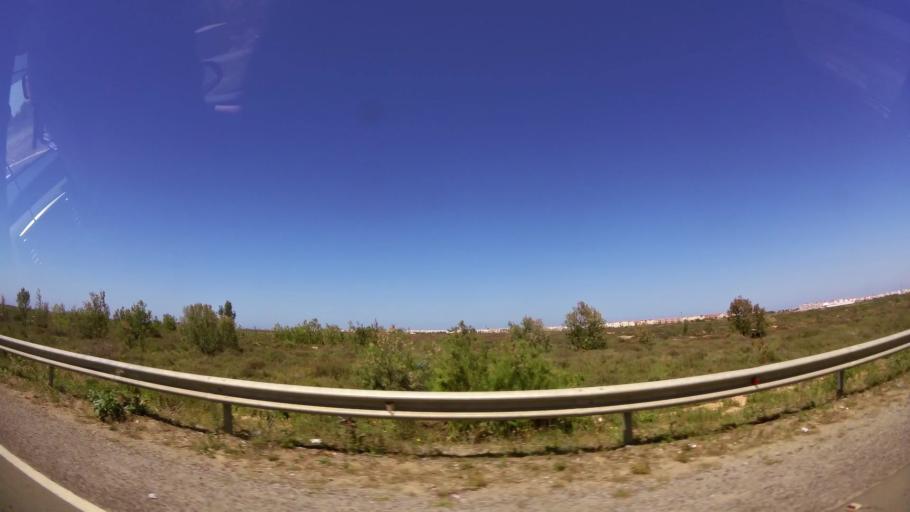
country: MA
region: Oriental
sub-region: Berkane-Taourirt
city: Madagh
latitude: 35.0995
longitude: -2.3231
